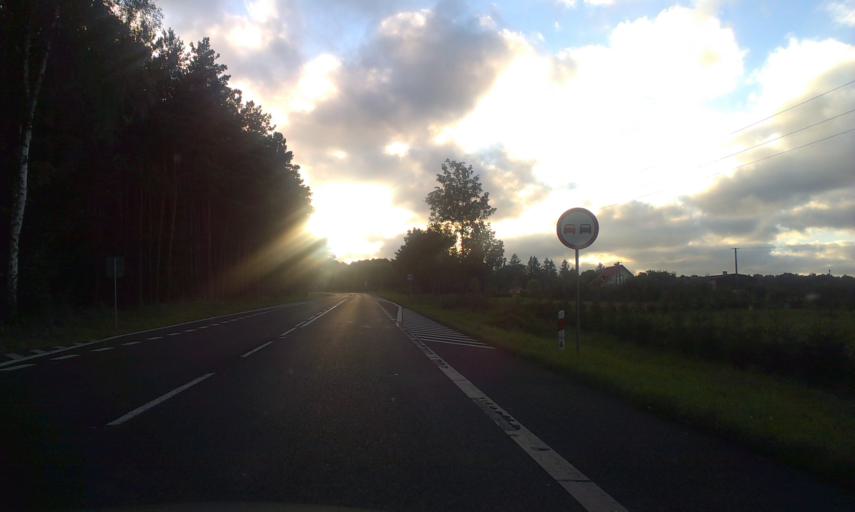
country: PL
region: West Pomeranian Voivodeship
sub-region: Powiat slawienski
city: Darlowo
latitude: 54.2787
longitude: 16.4635
